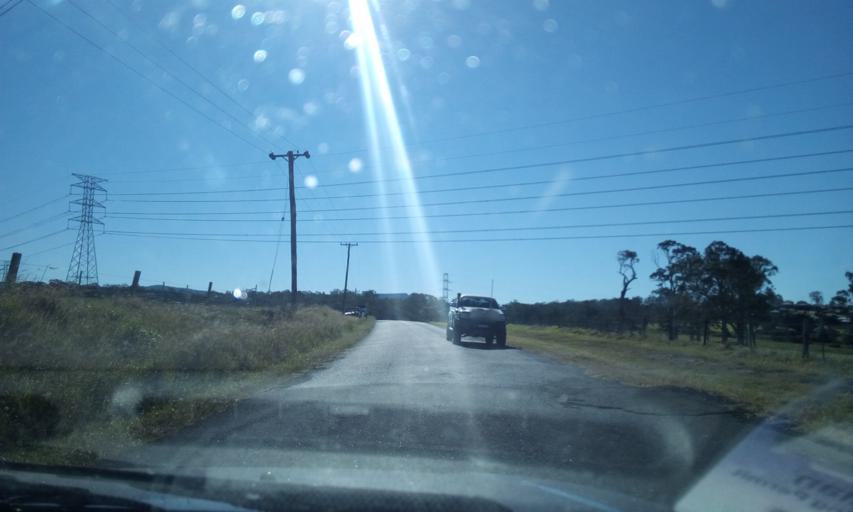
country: AU
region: New South Wales
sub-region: Wollongong
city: Dapto
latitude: -34.5248
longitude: 150.7780
